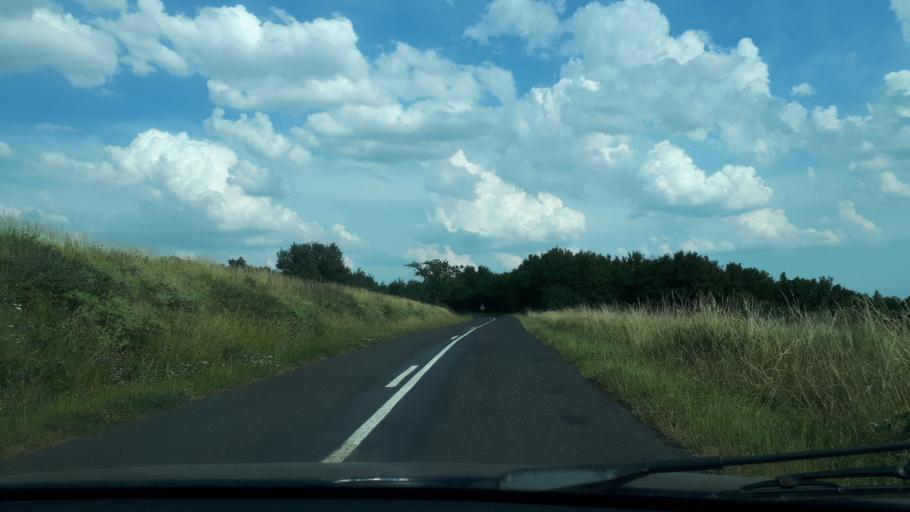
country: FR
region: Pays de la Loire
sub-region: Departement de la Sarthe
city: Besse-sur-Braye
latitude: 47.7781
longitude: 0.7883
